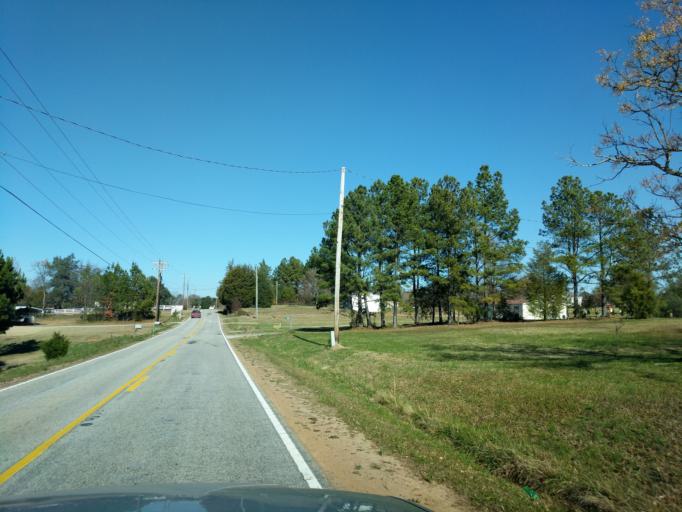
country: US
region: South Carolina
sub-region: Spartanburg County
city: Inman Mills
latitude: 35.0517
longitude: -82.1800
